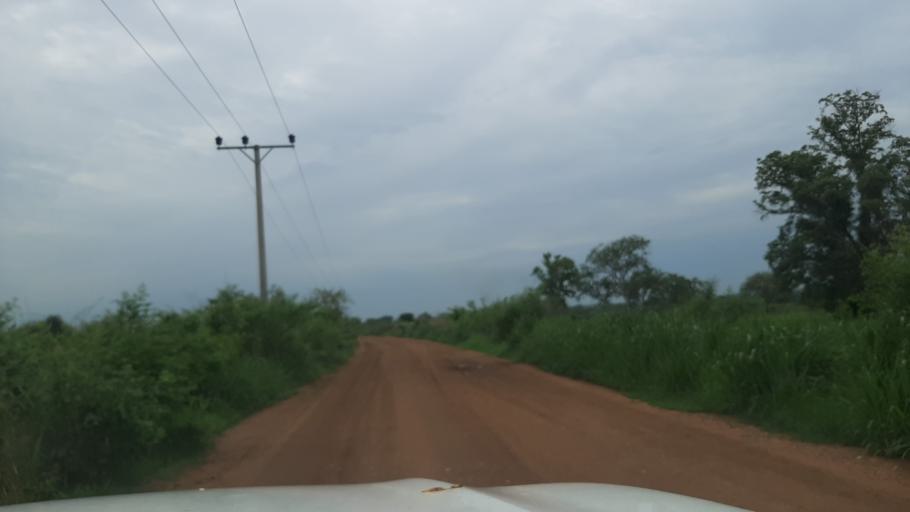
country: ET
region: Gambela
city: Gambela
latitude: 8.2161
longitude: 34.5506
